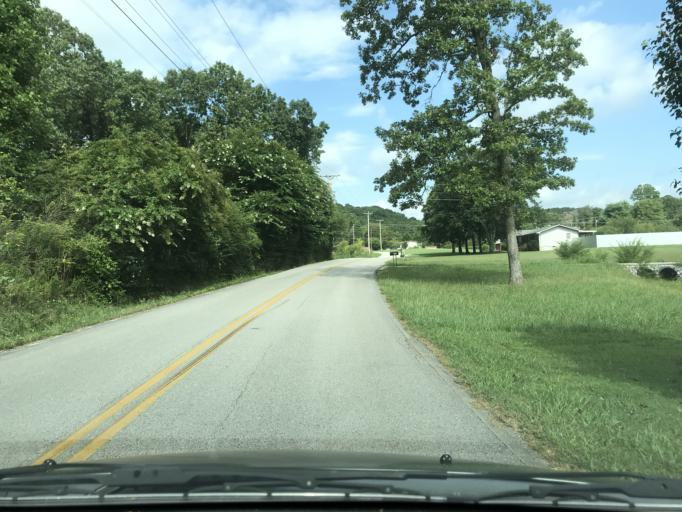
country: US
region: Tennessee
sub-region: Hamilton County
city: Lakesite
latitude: 35.1814
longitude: -85.0716
